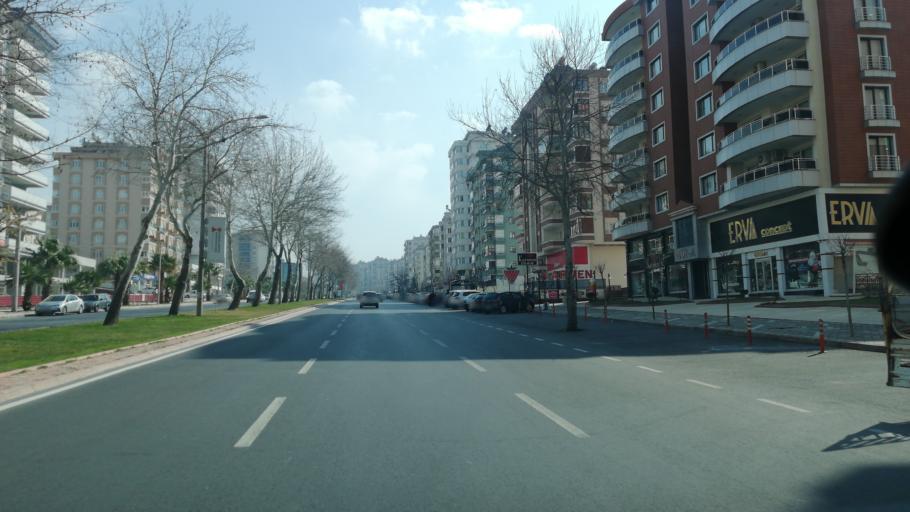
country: TR
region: Kahramanmaras
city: Kahramanmaras
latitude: 37.5907
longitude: 36.8712
